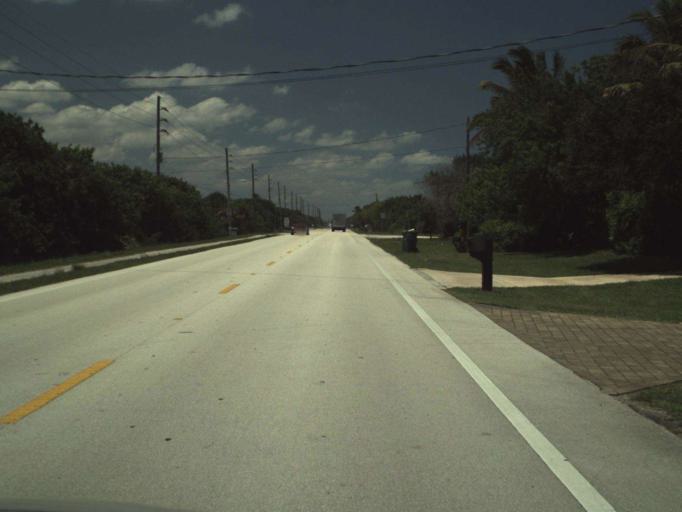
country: US
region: Florida
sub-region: Brevard County
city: Micco
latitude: 27.8854
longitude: -80.4617
